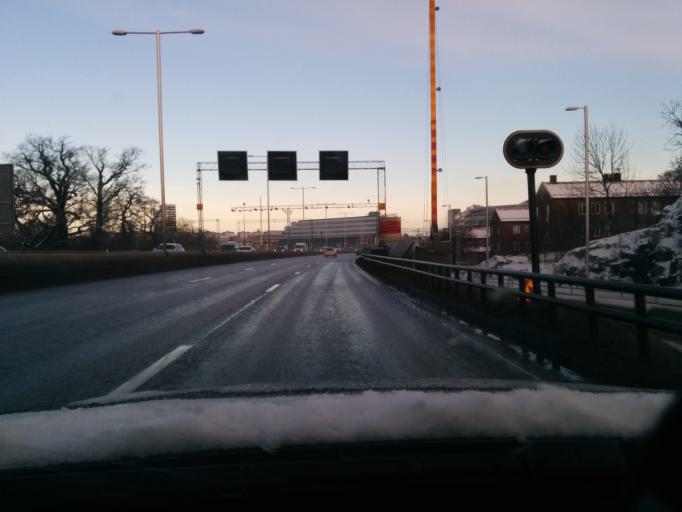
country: SE
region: Stockholm
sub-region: Solna Kommun
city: Solna
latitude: 59.3328
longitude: 18.0101
